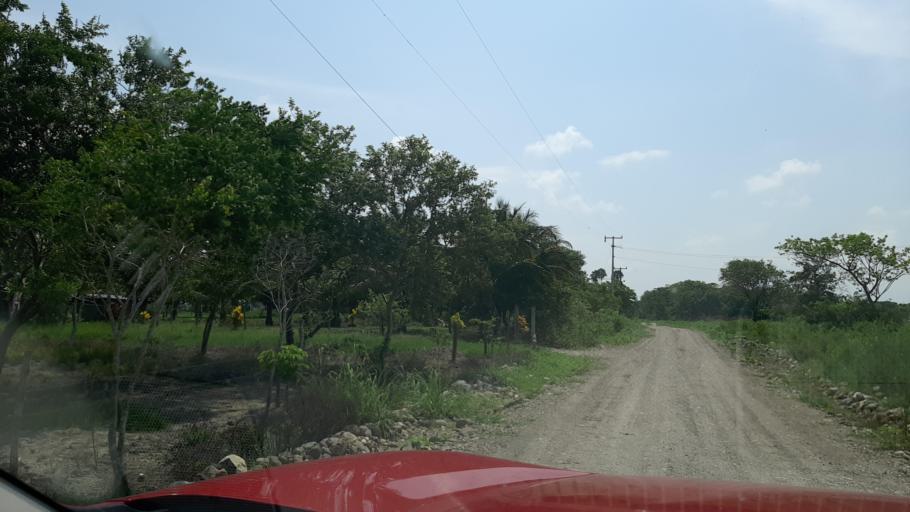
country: MX
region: Veracruz
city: Nautla
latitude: 20.2487
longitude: -96.8003
